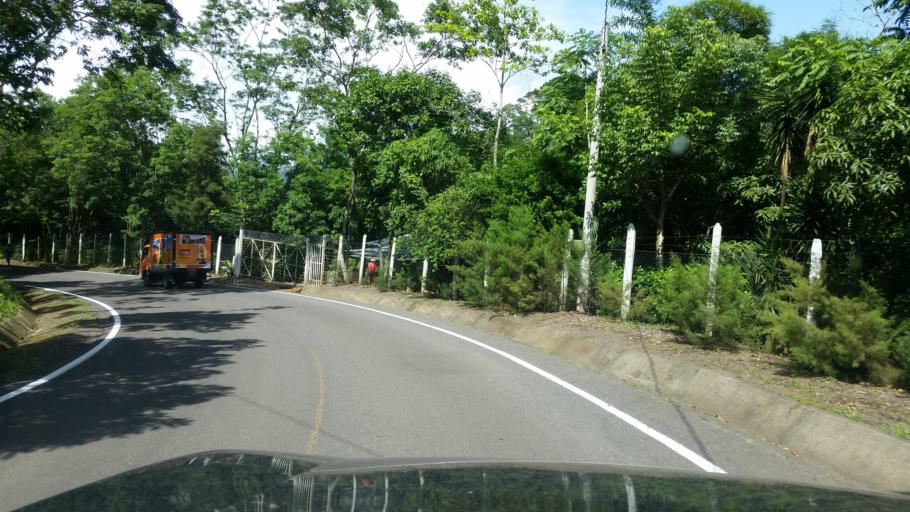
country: NI
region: Matagalpa
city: San Ramon
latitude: 12.9958
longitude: -85.8179
